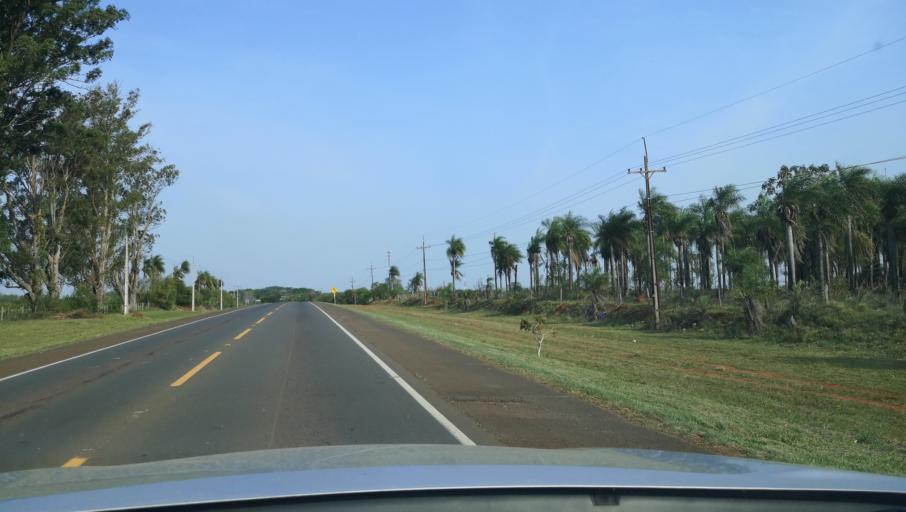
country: PY
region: Misiones
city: San Patricio
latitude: -26.9640
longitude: -56.8343
